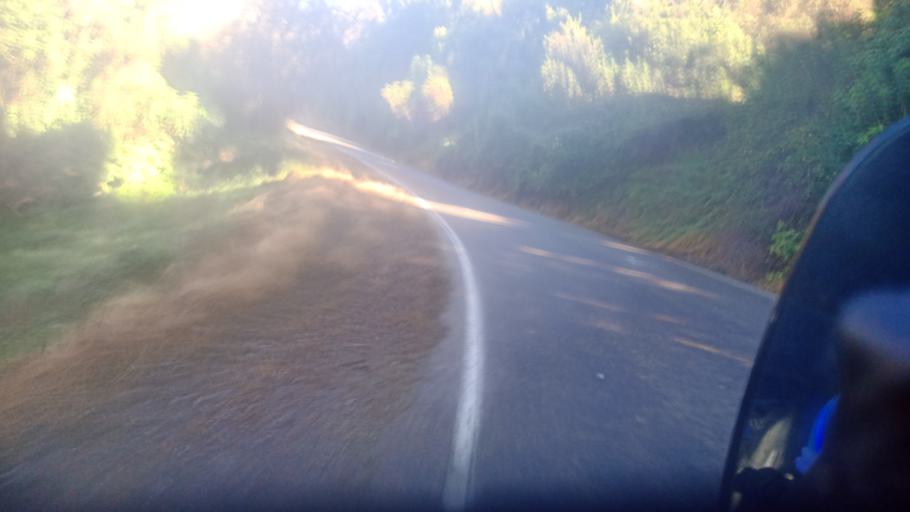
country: NZ
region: Gisborne
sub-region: Gisborne District
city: Gisborne
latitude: -38.5603
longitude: 177.6195
